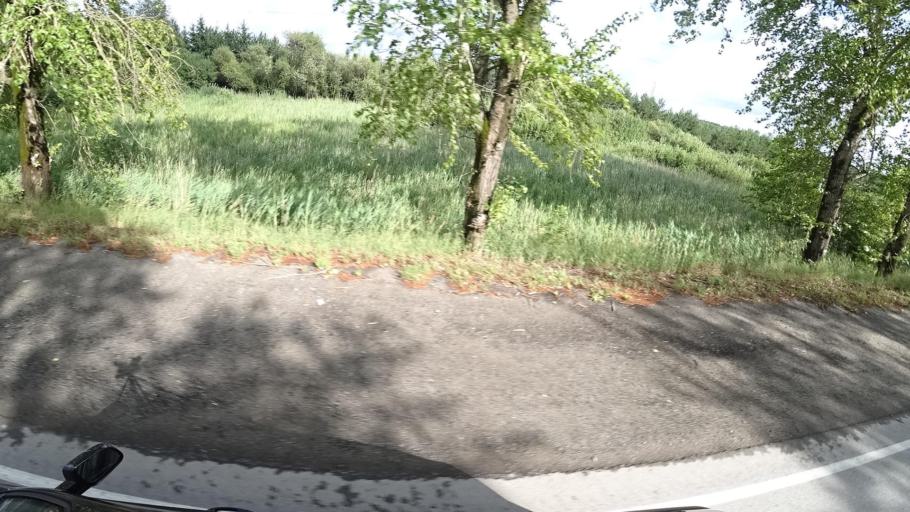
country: RU
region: Sverdlovsk
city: Kamyshlov
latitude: 56.8359
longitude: 62.6975
